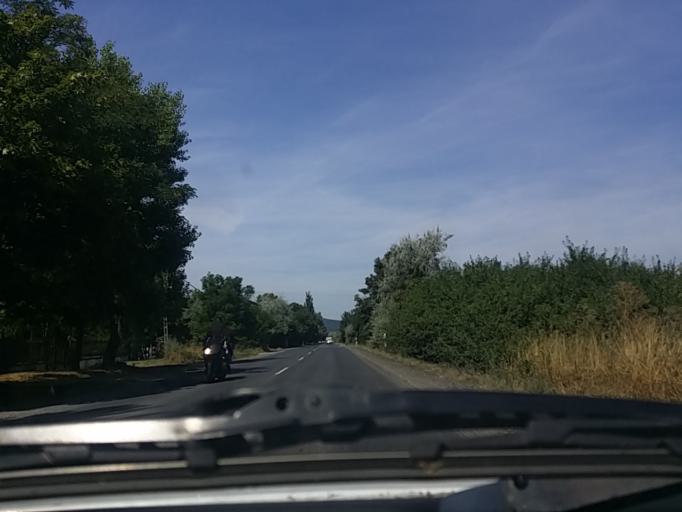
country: HU
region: Pest
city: Solymar
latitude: 47.6093
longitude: 18.9392
